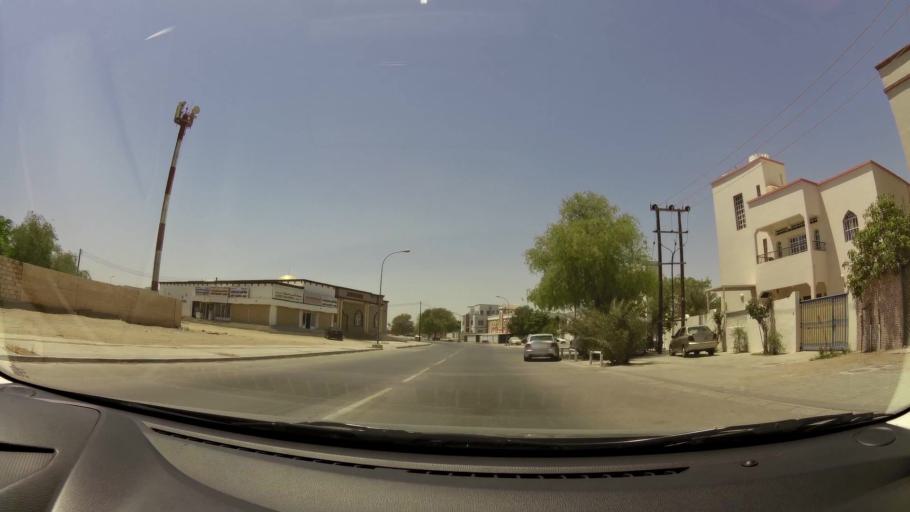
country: OM
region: Muhafazat Masqat
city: As Sib al Jadidah
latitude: 23.6291
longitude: 58.2415
